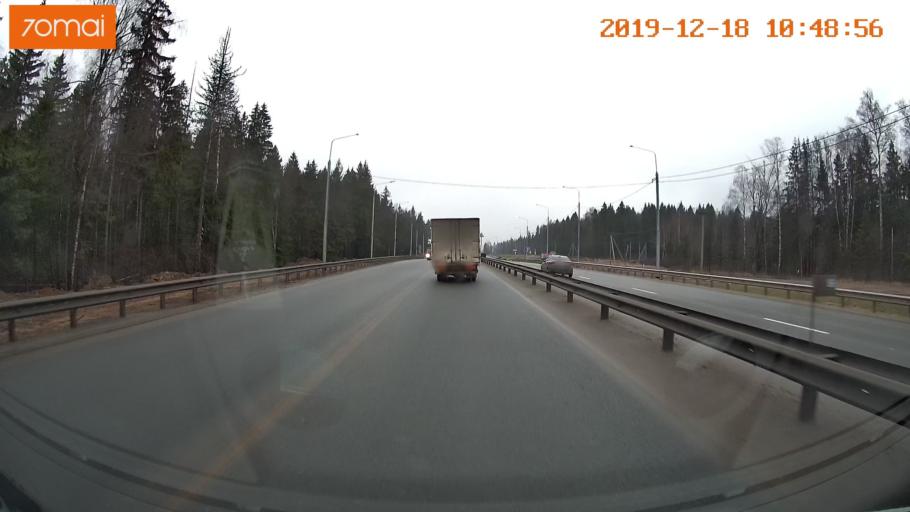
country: RU
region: Moskovskaya
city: Selyatino
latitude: 55.5002
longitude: 37.0216
